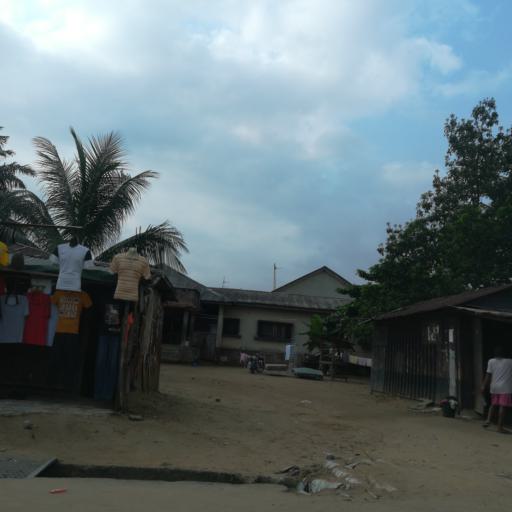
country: NG
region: Rivers
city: Okrika
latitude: 4.7834
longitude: 7.1405
